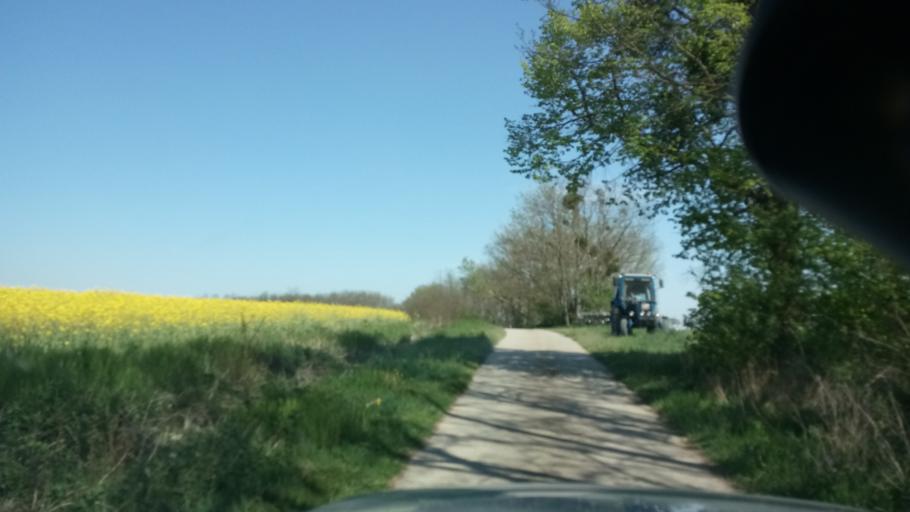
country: HU
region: Zala
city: Sarmellek
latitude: 46.7033
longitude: 17.0930
